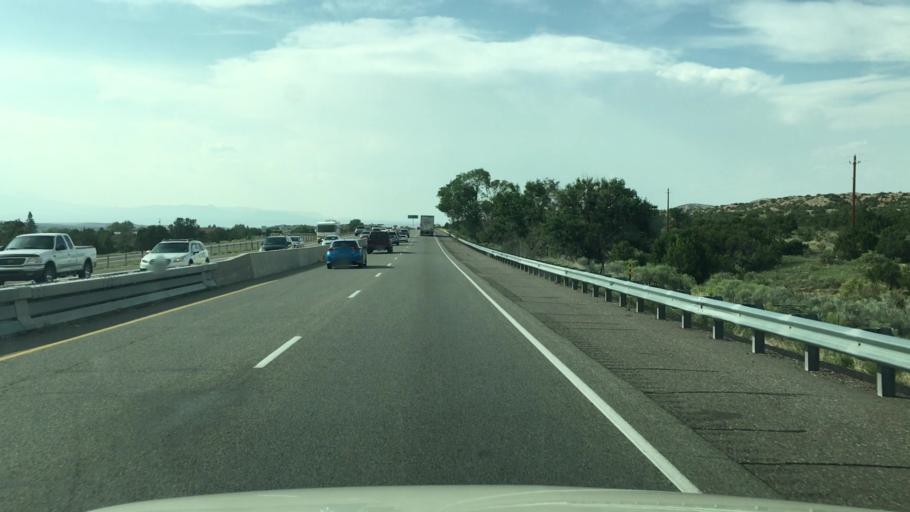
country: US
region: New Mexico
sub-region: Santa Fe County
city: Nambe
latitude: 35.7976
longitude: -105.9575
